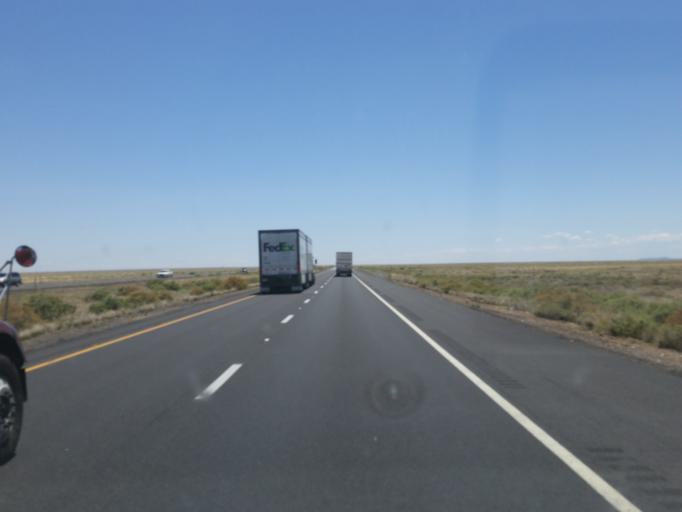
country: US
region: Arizona
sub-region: Coconino County
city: Flagstaff
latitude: 35.1502
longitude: -111.2419
